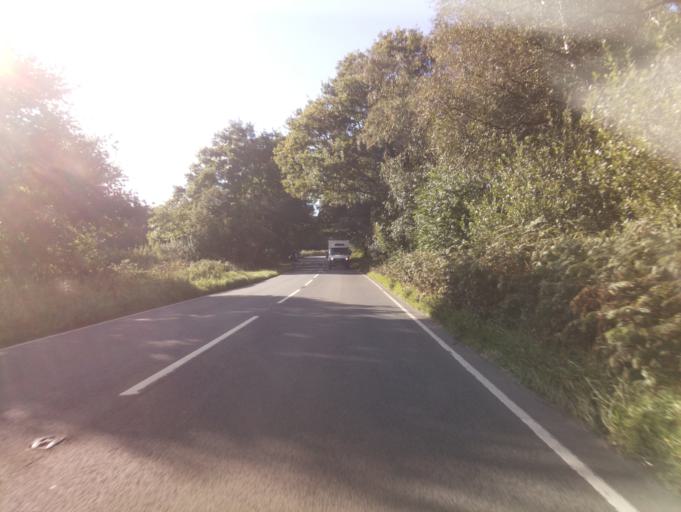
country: GB
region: England
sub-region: Devon
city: Newton Poppleford
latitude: 50.7015
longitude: -3.3408
